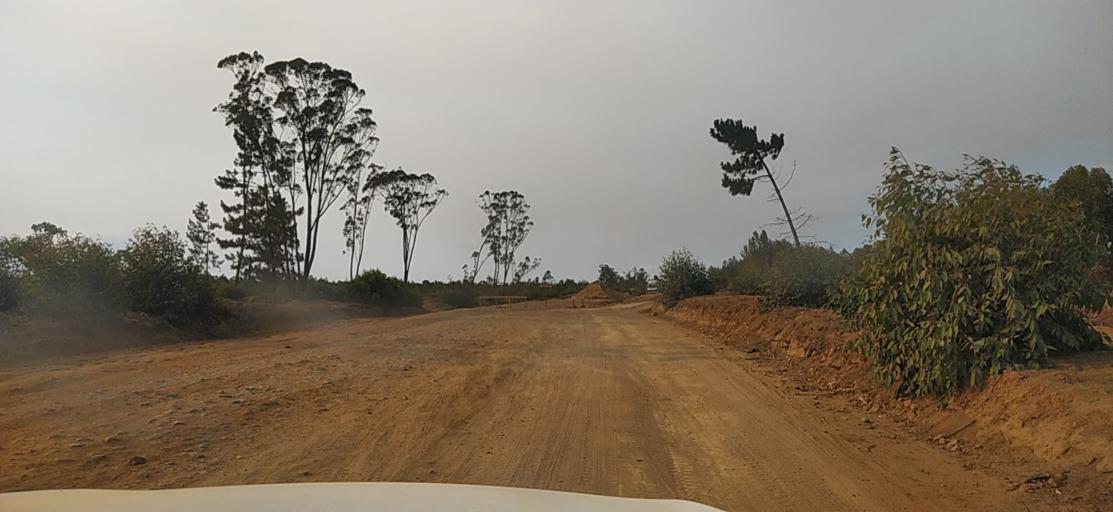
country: MG
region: Alaotra Mangoro
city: Moramanga
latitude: -18.6197
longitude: 48.2766
